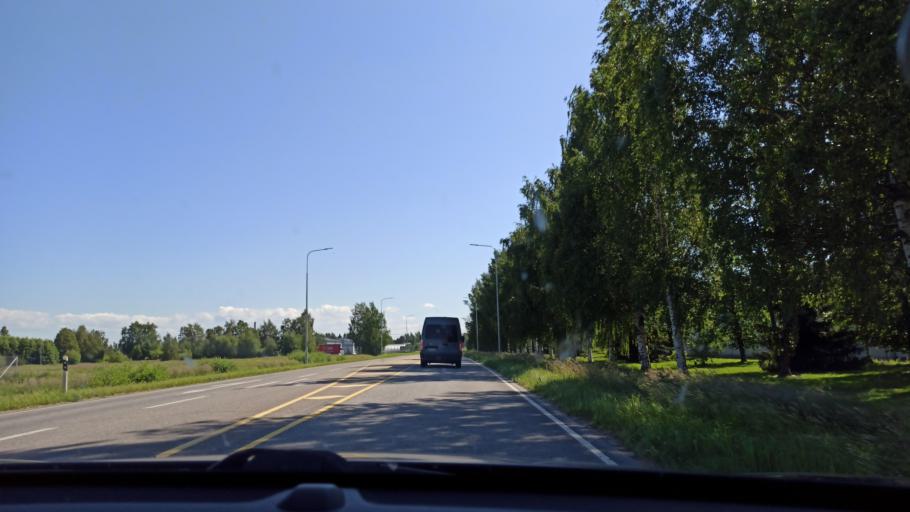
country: FI
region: Satakunta
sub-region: Pori
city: Pori
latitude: 61.5121
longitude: 21.8033
